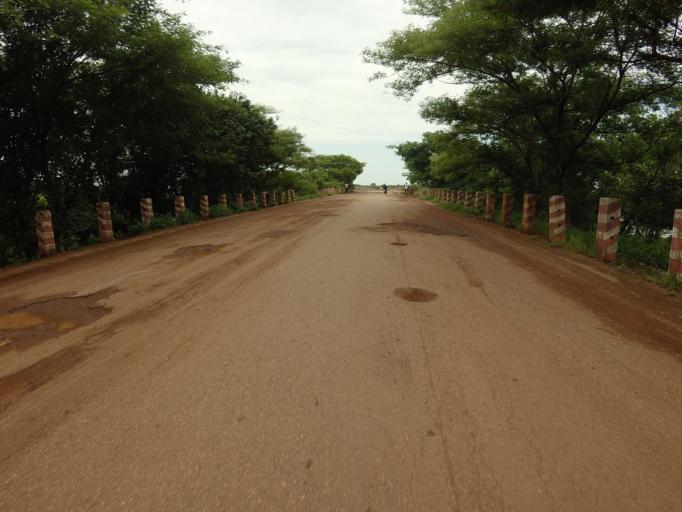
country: GH
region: Upper East
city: Bawku
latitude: 11.0026
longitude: -0.3858
